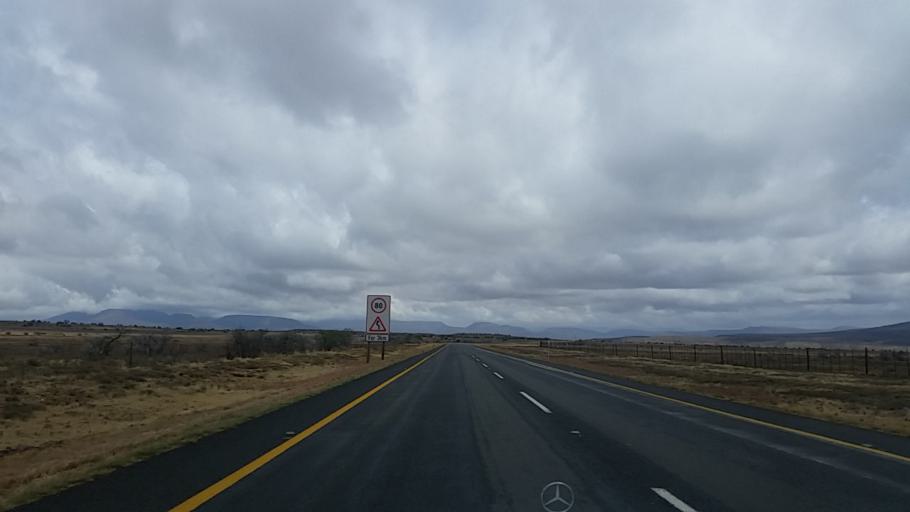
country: ZA
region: Eastern Cape
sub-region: Cacadu District Municipality
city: Graaff-Reinet
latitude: -32.1297
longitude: 24.5890
